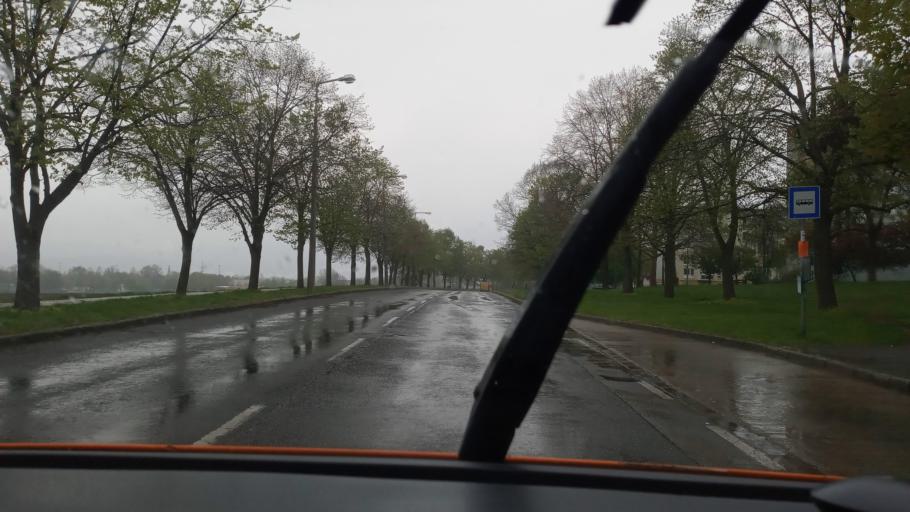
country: HU
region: Baranya
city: Pecs
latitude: 46.0311
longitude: 18.2124
